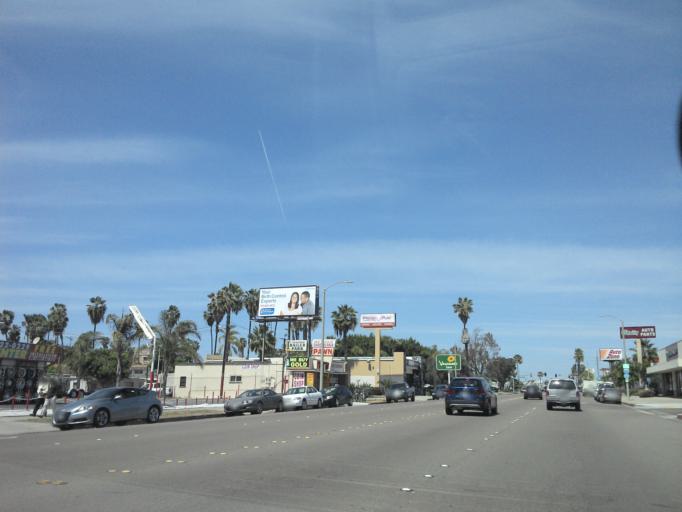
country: US
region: California
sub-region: San Diego County
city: Chula Vista
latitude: 32.6391
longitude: -117.0926
